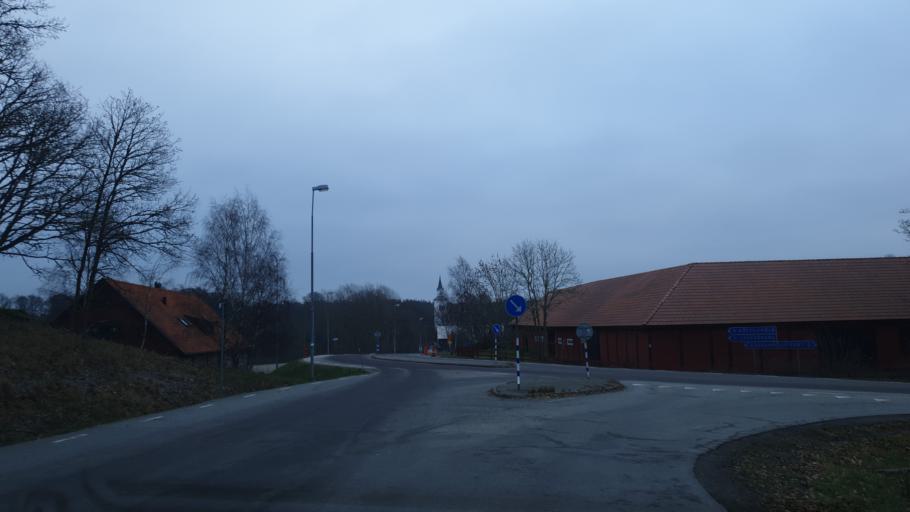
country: SE
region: Blekinge
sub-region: Karlskrona Kommun
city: Rodeby
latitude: 56.2174
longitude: 15.6682
